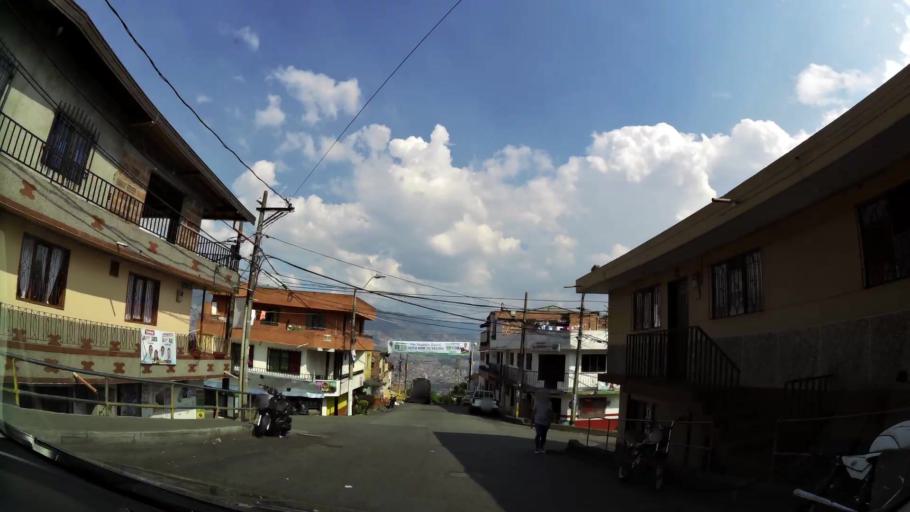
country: CO
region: Antioquia
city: Medellin
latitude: 6.2892
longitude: -75.5946
